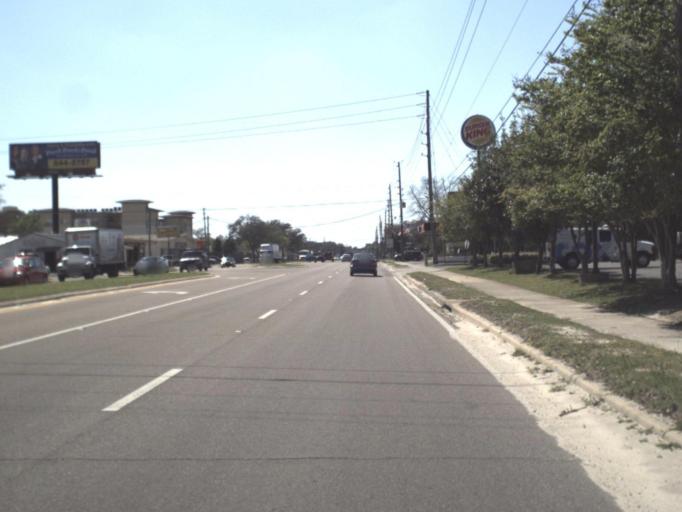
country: US
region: Florida
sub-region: Okaloosa County
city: Wright
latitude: 30.4494
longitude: -86.6257
